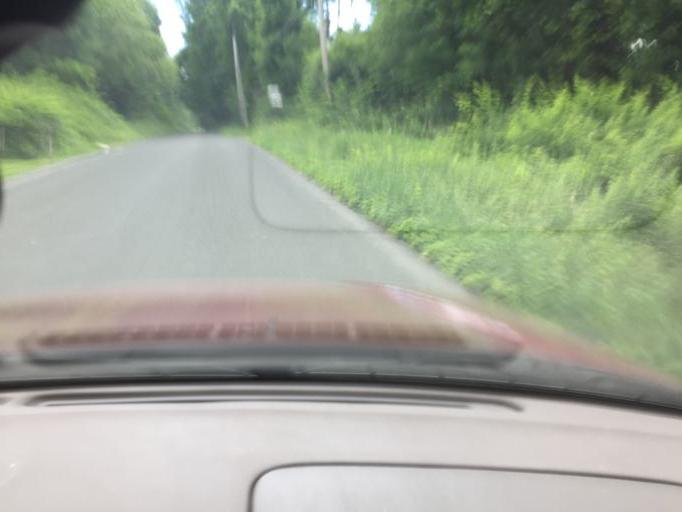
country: US
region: Connecticut
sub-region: Litchfield County
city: Litchfield
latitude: 41.7696
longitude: -73.2541
